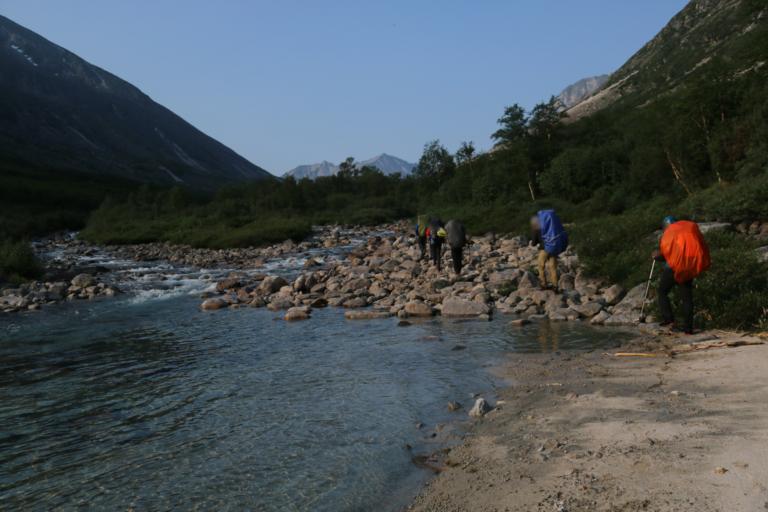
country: RU
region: Respublika Buryatiya
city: Novyy Uoyan
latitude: 56.2604
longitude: 111.0919
